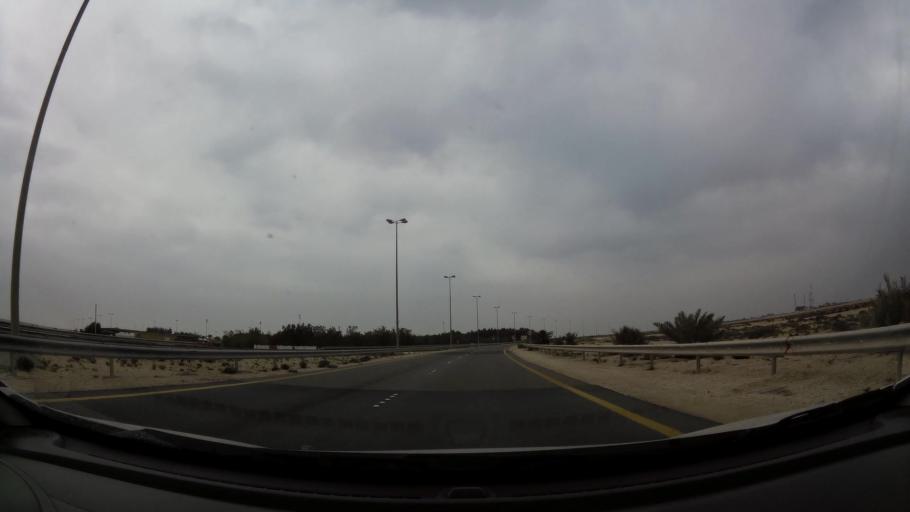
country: BH
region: Central Governorate
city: Dar Kulayb
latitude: 25.9946
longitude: 50.4818
